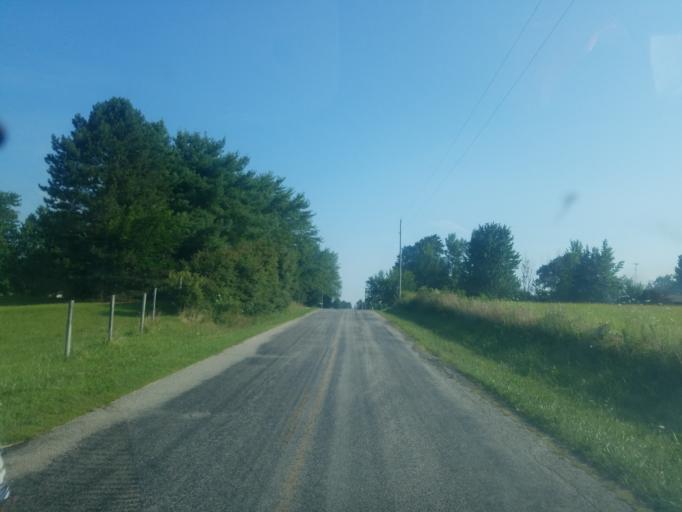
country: US
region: Ohio
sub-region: Richland County
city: Shelby
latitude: 40.8384
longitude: -82.6775
